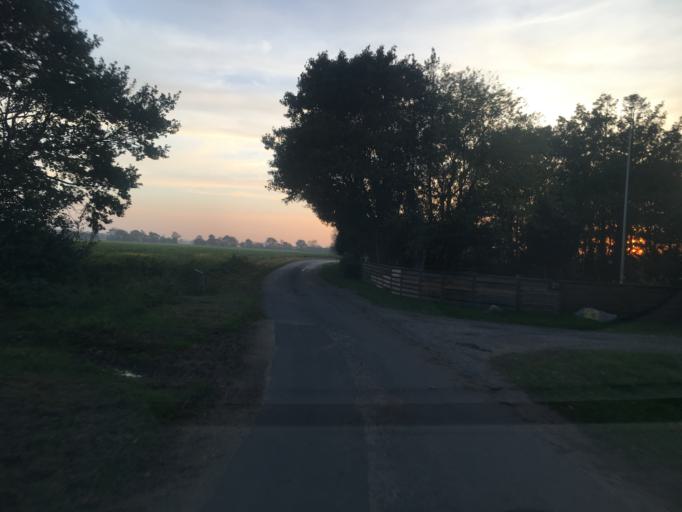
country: DE
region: Schleswig-Holstein
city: Bramstedtlund
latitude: 54.9852
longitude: 9.0806
